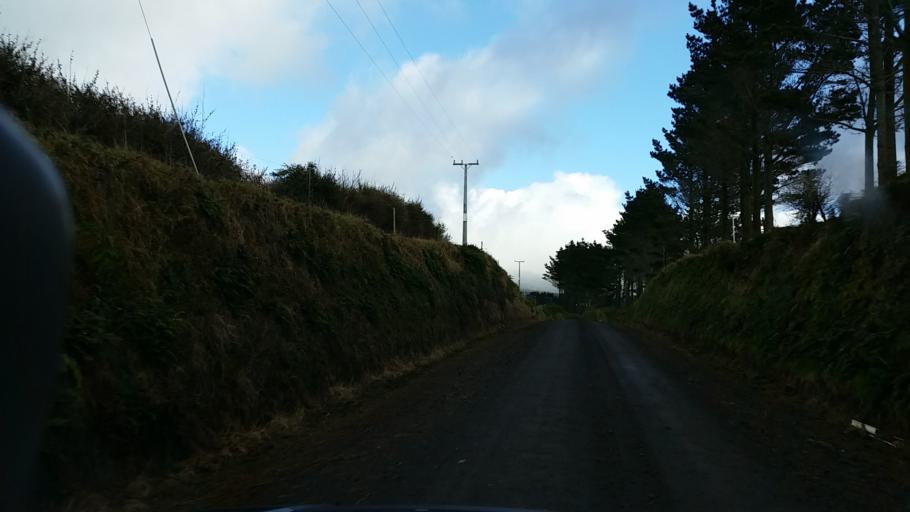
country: NZ
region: Taranaki
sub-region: South Taranaki District
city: Eltham
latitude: -39.3380
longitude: 174.1853
